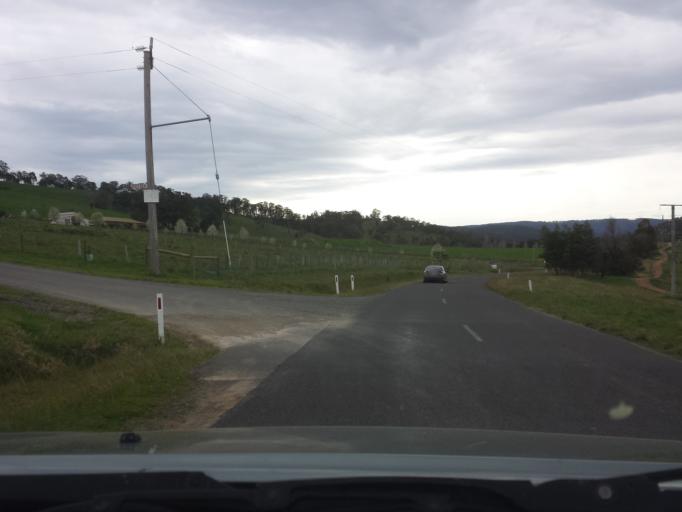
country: AU
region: Victoria
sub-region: Yarra Ranges
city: Yarra Glen
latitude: -37.6324
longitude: 145.3734
